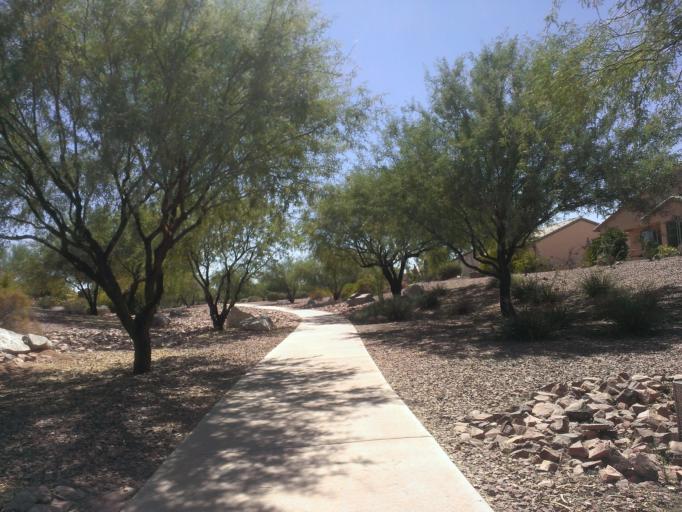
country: US
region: Arizona
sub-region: Pinal County
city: Arizona City
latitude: 32.8121
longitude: -111.6368
